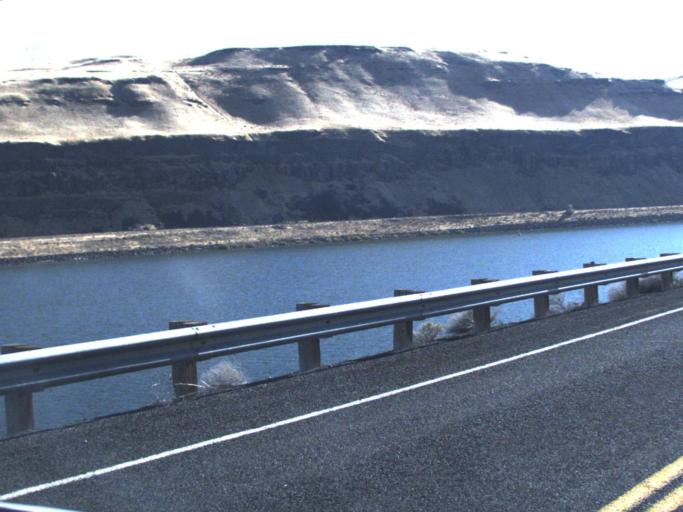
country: US
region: Washington
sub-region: Franklin County
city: Connell
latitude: 46.5407
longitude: -118.5616
